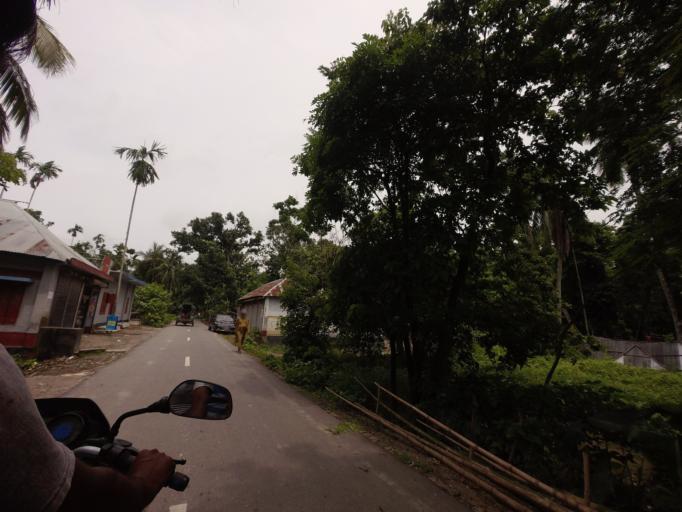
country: BD
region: Khulna
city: Kalia
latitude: 23.0862
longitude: 89.6681
